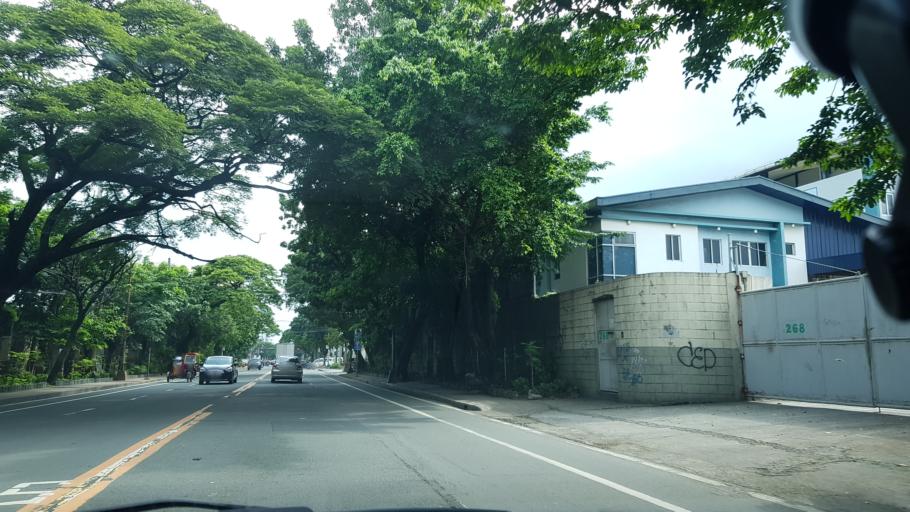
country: PH
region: Metro Manila
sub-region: Pasig
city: Pasig City
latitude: 14.5790
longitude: 121.0864
